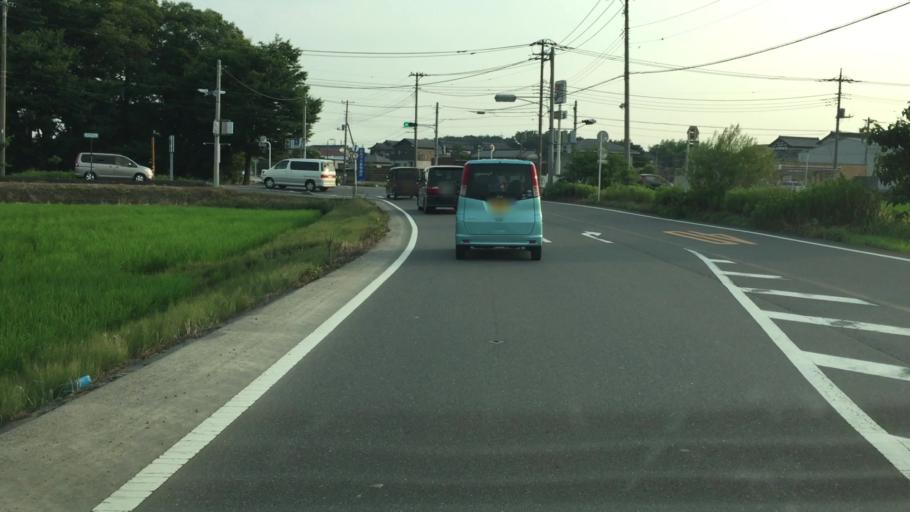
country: JP
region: Gunma
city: Tatebayashi
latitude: 36.2374
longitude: 139.5916
